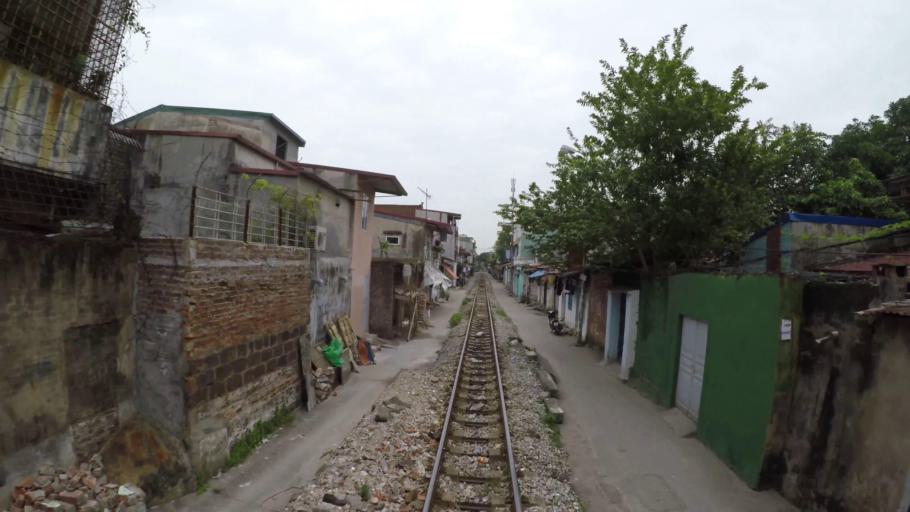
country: VN
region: Hai Phong
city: Haiphong
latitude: 20.8619
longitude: 106.6618
